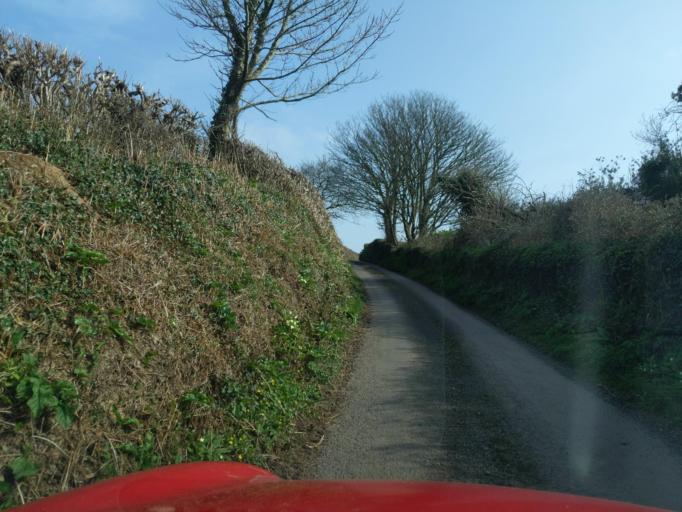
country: GB
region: England
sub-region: Devon
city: Kingsbridge
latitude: 50.2916
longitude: -3.7368
